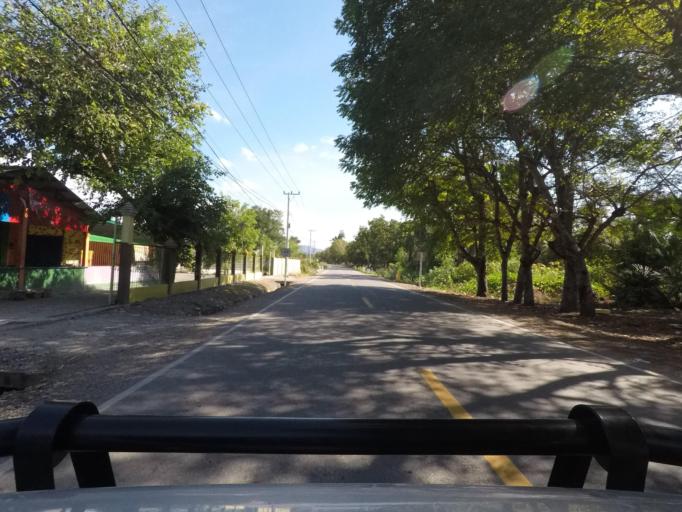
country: ID
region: East Nusa Tenggara
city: Atambua
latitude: -8.9513
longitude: 124.9631
